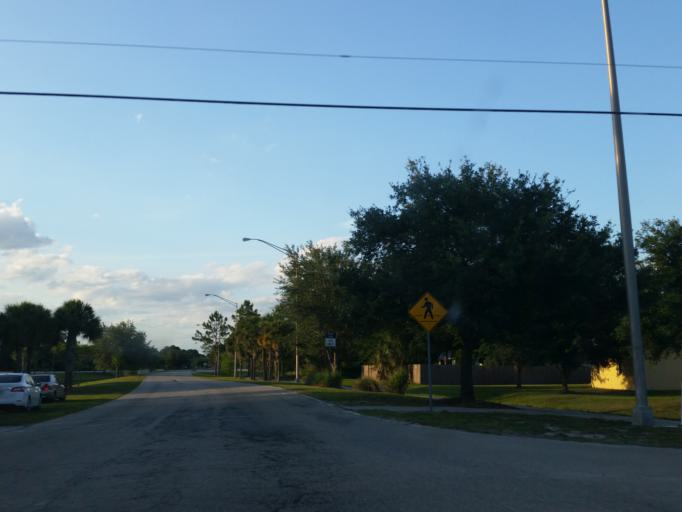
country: US
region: Florida
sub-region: Sarasota County
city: North Port
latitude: 27.0848
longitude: -82.2085
